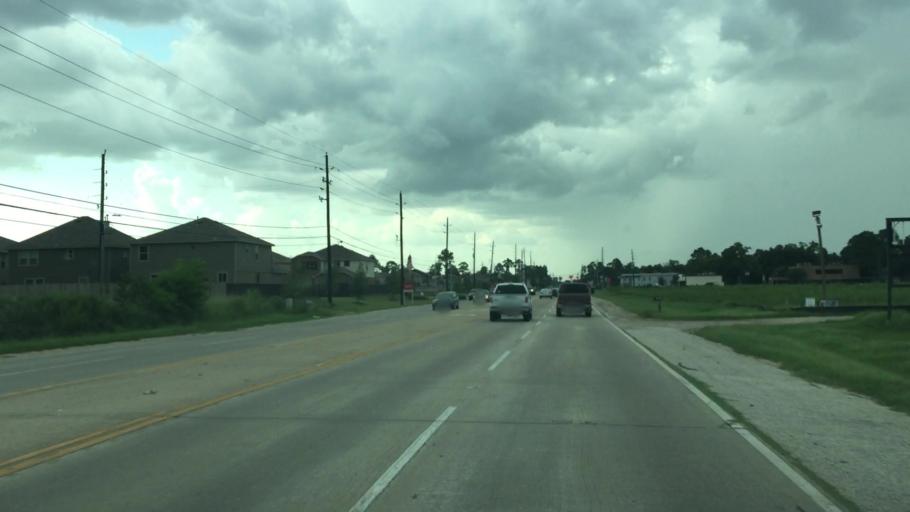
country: US
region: Texas
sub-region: Harris County
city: Hudson
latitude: 29.9960
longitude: -95.5043
